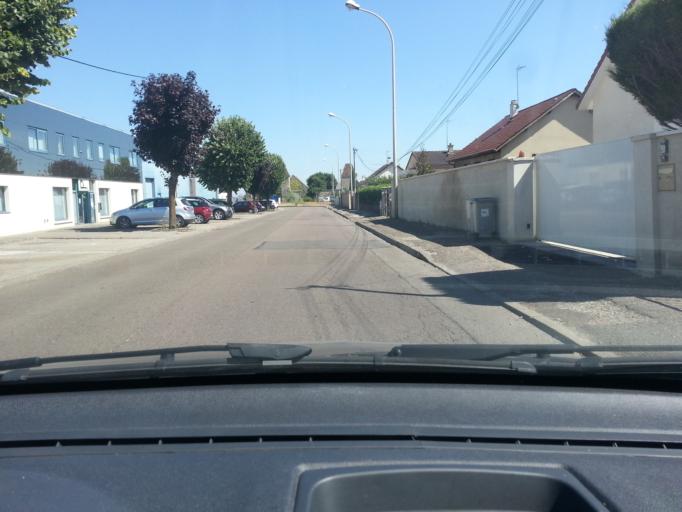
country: FR
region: Bourgogne
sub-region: Departement de la Cote-d'Or
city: Perrigny-les-Dijon
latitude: 47.2780
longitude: 5.0115
